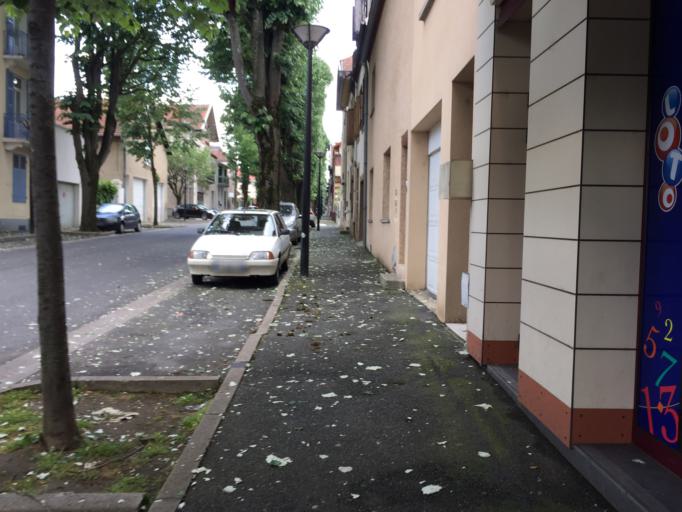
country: FR
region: Auvergne
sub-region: Departement de l'Allier
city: Vichy
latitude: 46.1269
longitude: 3.4343
